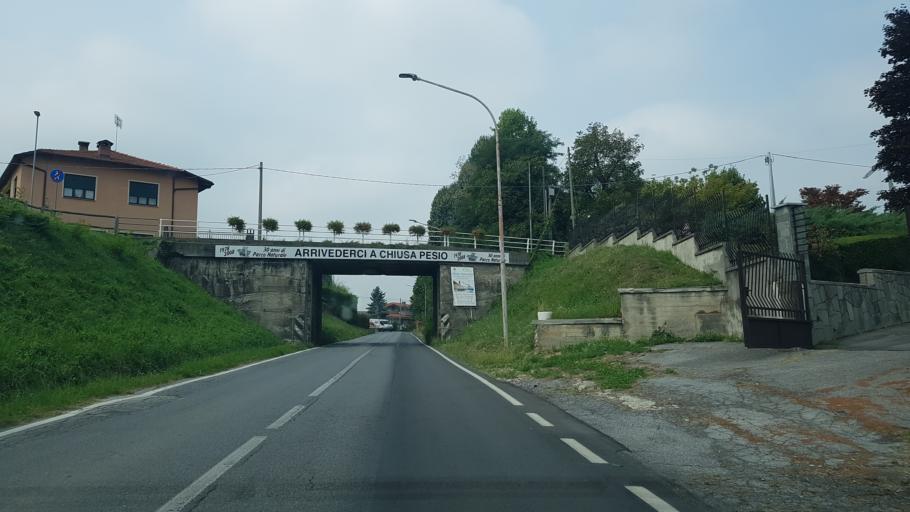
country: IT
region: Piedmont
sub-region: Provincia di Cuneo
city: Chiusa di Pesio
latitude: 44.3279
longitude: 7.6726
